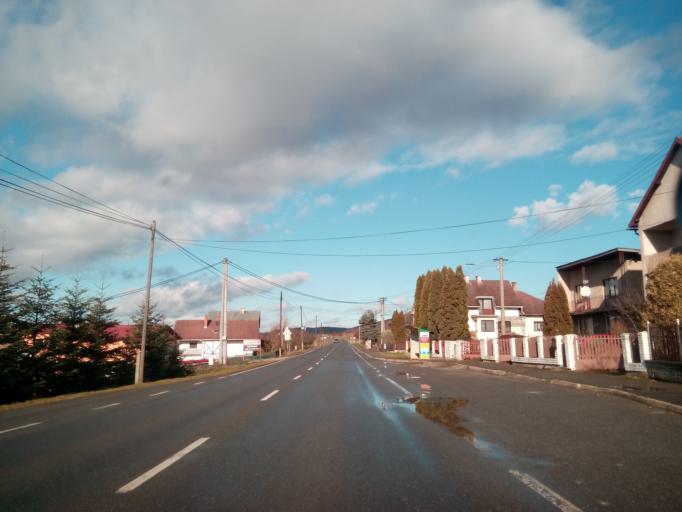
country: SK
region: Presovsky
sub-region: Okres Bardejov
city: Bardejov
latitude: 49.2188
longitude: 21.2942
